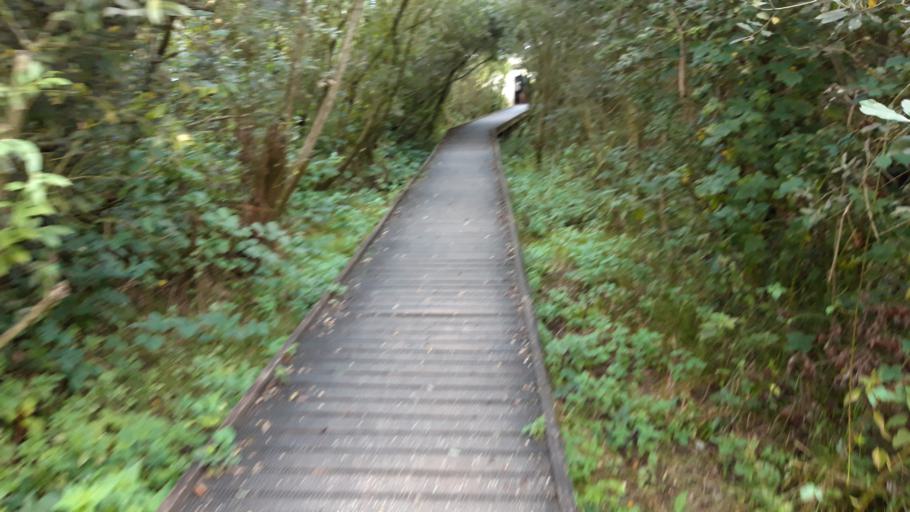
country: NL
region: Friesland
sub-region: Gemeente Schiermonnikoog
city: Schiermonnikoog
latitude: 53.4716
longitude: 6.1513
